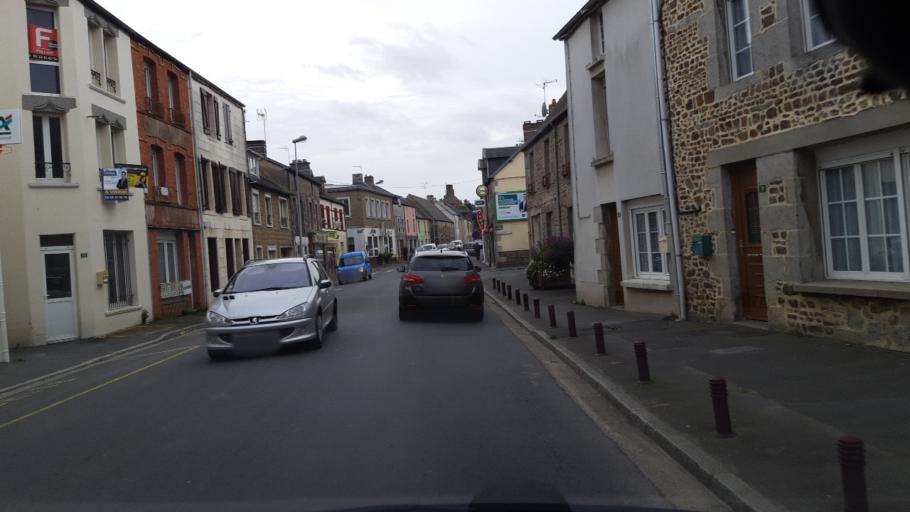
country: FR
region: Lower Normandy
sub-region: Departement de la Manche
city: Quettreville-sur-Sienne
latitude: 48.9160
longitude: -1.4360
